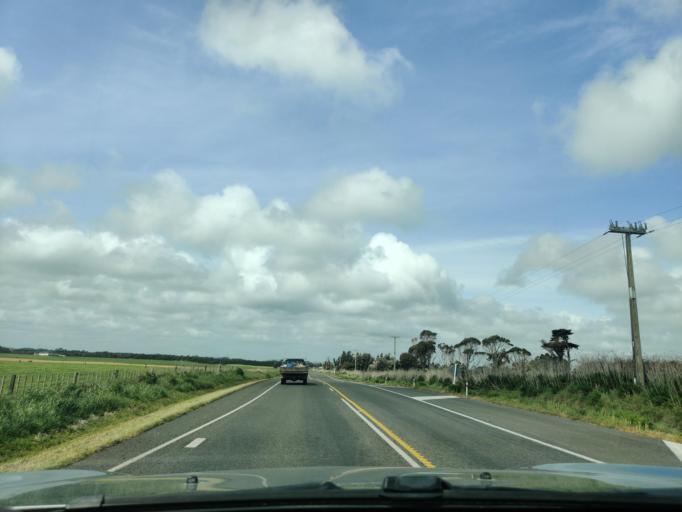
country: NZ
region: Taranaki
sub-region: South Taranaki District
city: Patea
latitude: -39.7673
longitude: 174.6060
